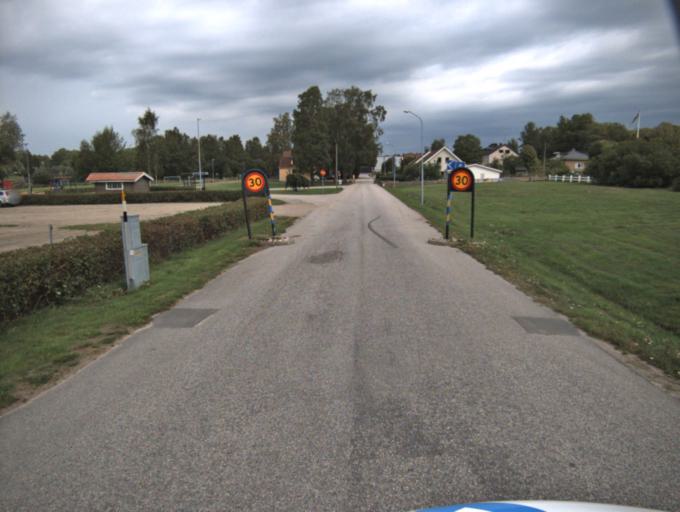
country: SE
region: Vaestra Goetaland
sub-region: Ulricehamns Kommun
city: Ulricehamn
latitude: 57.8409
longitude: 13.2848
